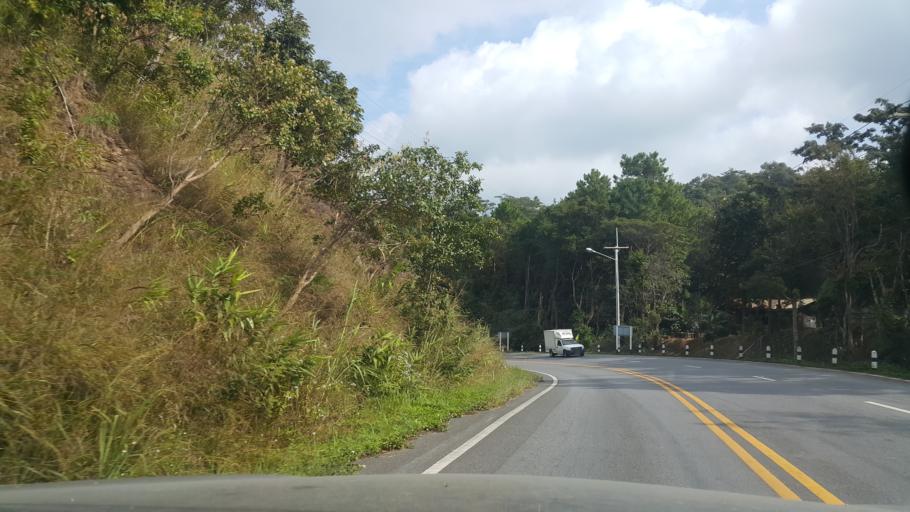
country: TH
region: Phayao
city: Phayao
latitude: 19.0605
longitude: 99.7794
